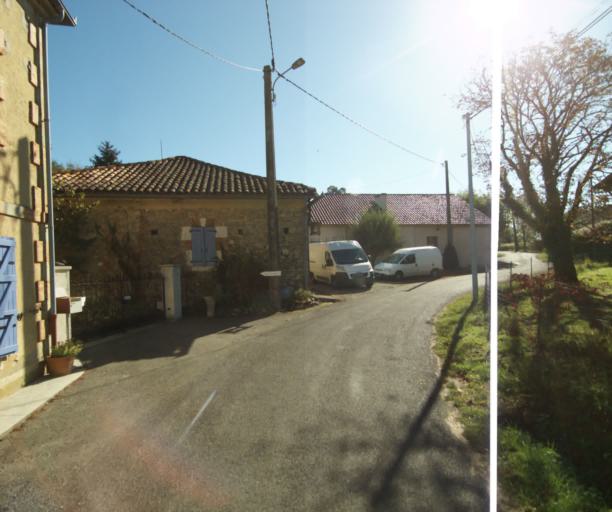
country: FR
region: Midi-Pyrenees
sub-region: Departement du Gers
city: Eauze
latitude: 43.8085
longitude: 0.1663
